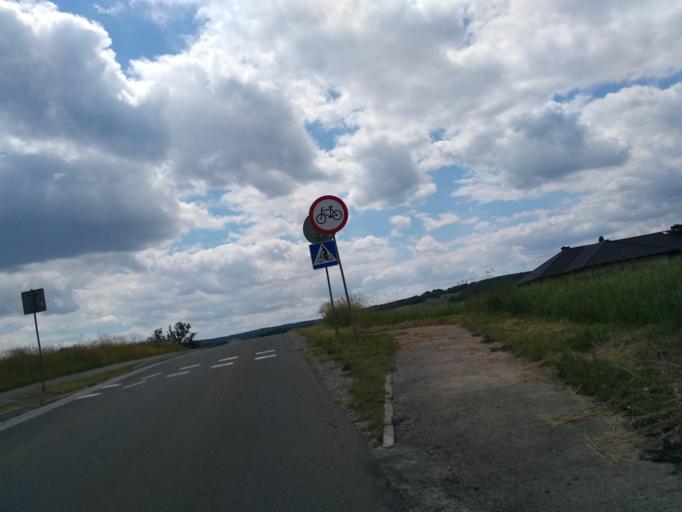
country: PL
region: Subcarpathian Voivodeship
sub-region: Powiat brzozowski
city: Nozdrzec
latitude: 49.7758
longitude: 22.2230
